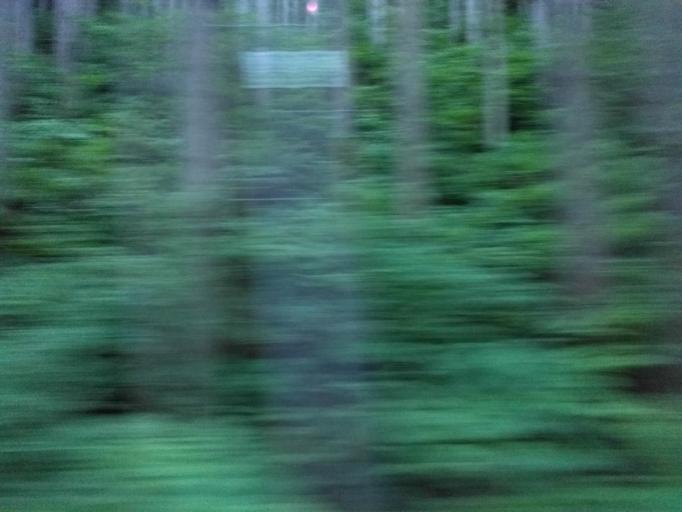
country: JP
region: Fukushima
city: Kitakata
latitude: 37.3693
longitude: 139.8047
